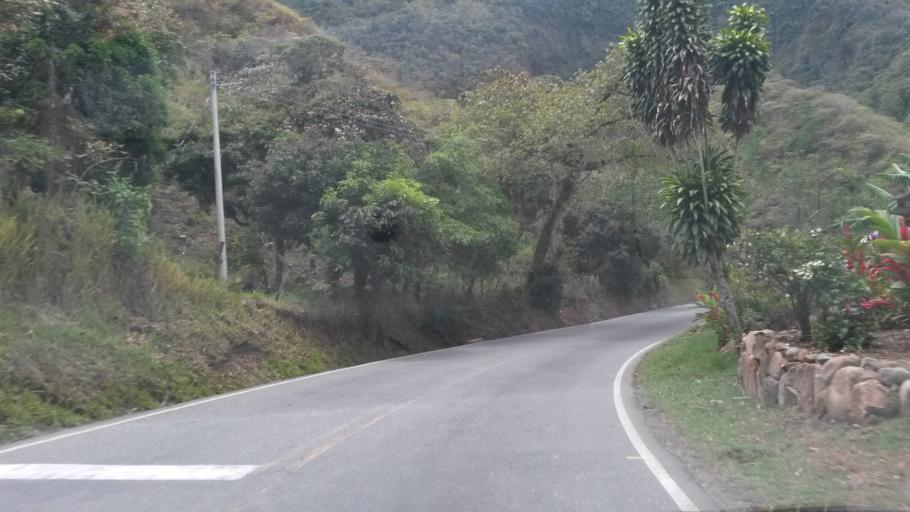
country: CO
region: Cauca
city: Rosas
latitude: 2.2513
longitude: -76.7628
